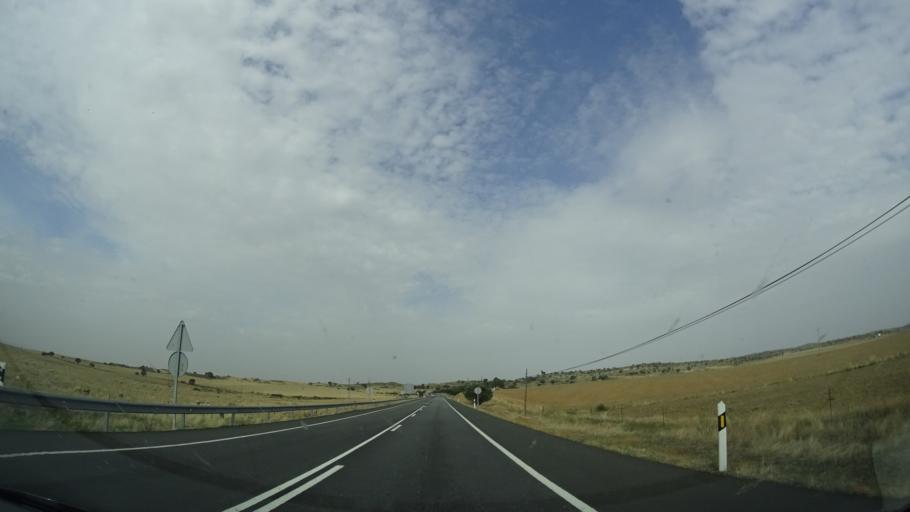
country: ES
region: Extremadura
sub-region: Provincia de Caceres
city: Trujillo
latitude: 39.4134
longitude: -5.8921
